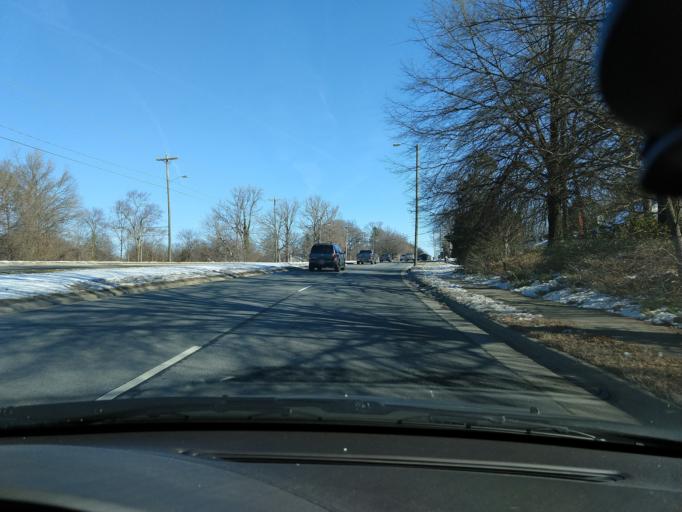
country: US
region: North Carolina
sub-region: Guilford County
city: Greensboro
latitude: 36.0484
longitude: -79.8105
